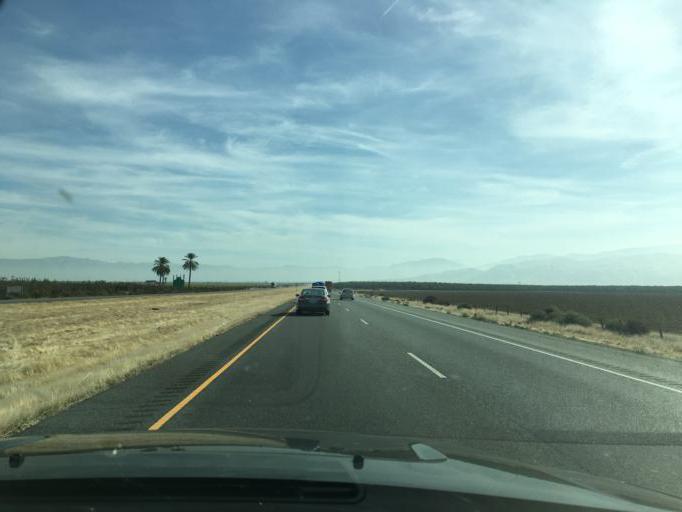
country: US
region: California
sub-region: Kern County
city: Greenfield
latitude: 35.0901
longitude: -119.0322
